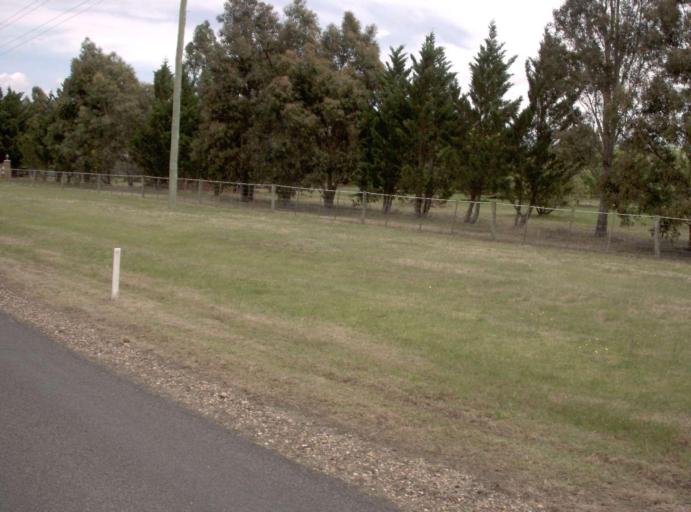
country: AU
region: Victoria
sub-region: Wellington
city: Sale
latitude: -37.9752
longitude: 147.0147
